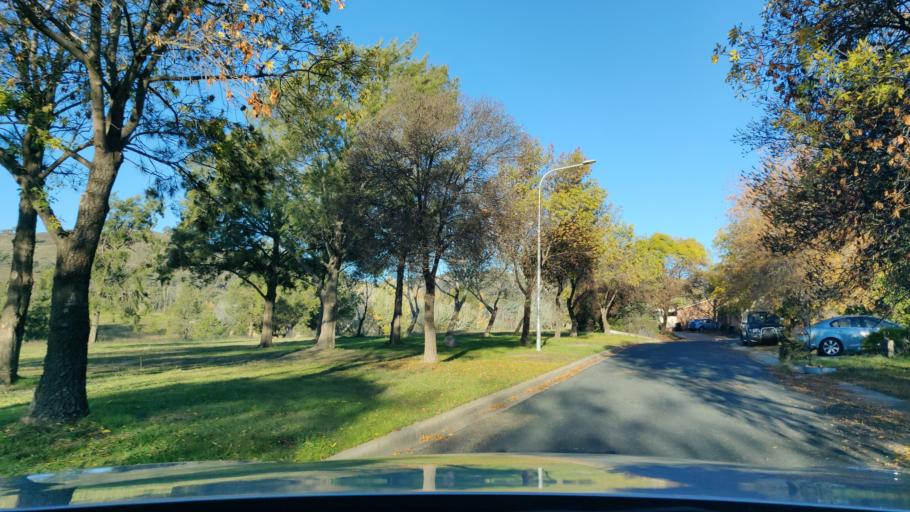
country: AU
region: Australian Capital Territory
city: Macarthur
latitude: -35.4397
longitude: 149.1240
